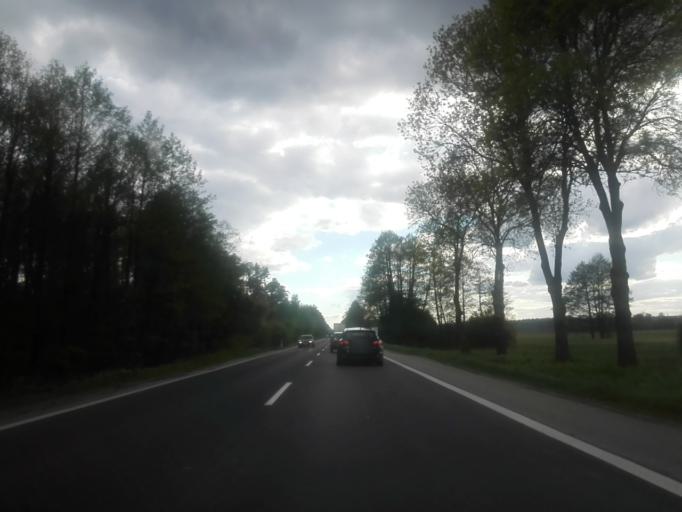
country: PL
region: Masovian Voivodeship
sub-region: Powiat ostrowski
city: Brok
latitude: 52.7529
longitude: 21.7856
